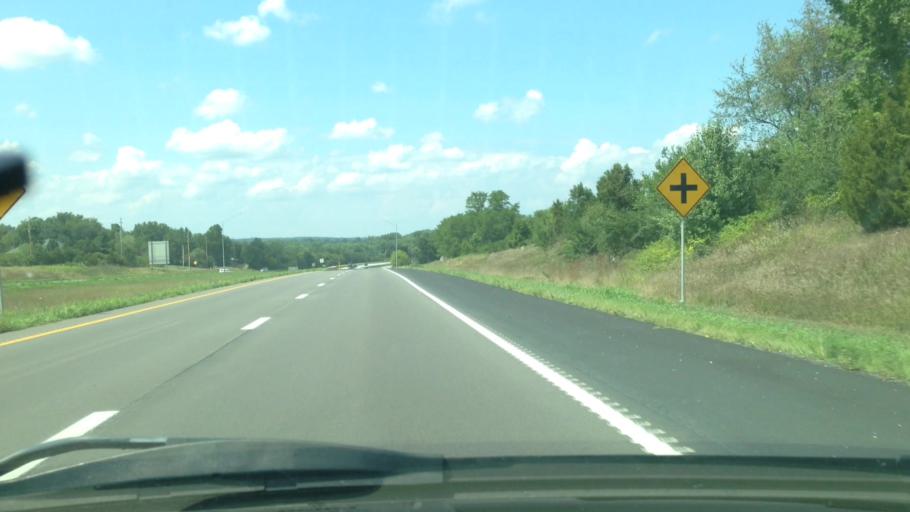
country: US
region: Missouri
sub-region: Lincoln County
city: Troy
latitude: 38.9999
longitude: -90.9722
